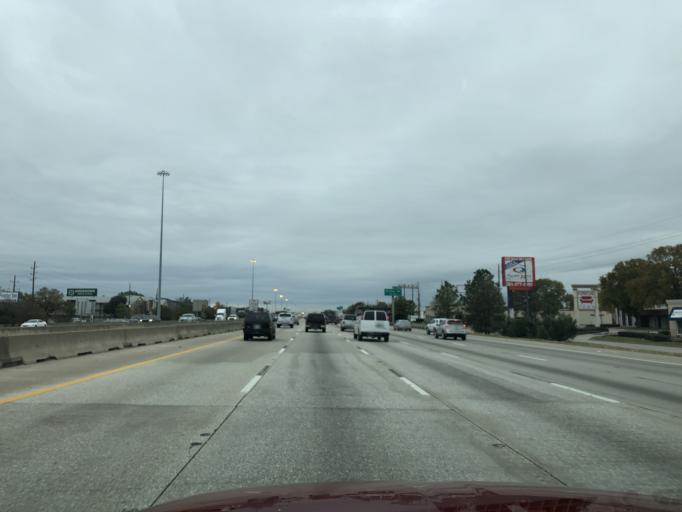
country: US
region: Texas
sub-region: Harris County
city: Spring
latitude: 30.0077
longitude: -95.4275
